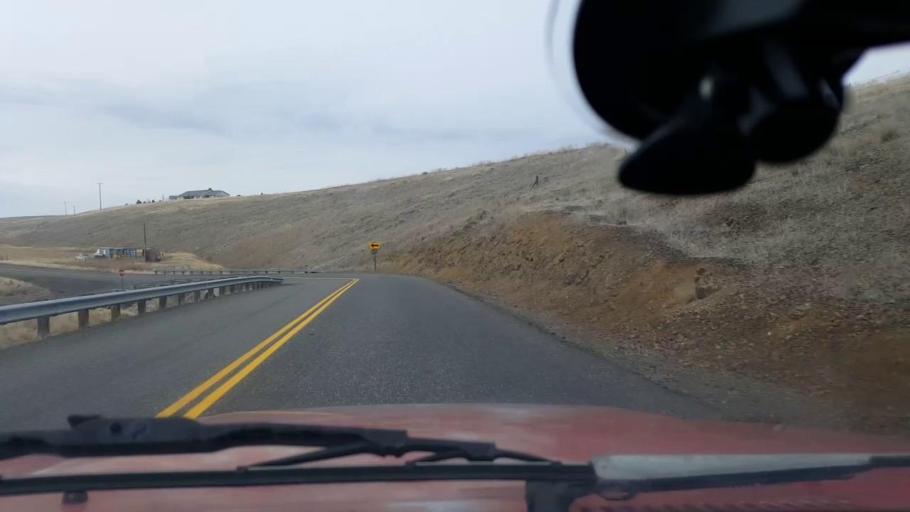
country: US
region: Washington
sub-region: Asotin County
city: Clarkston Heights-Vineland
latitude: 46.3779
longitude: -117.1474
